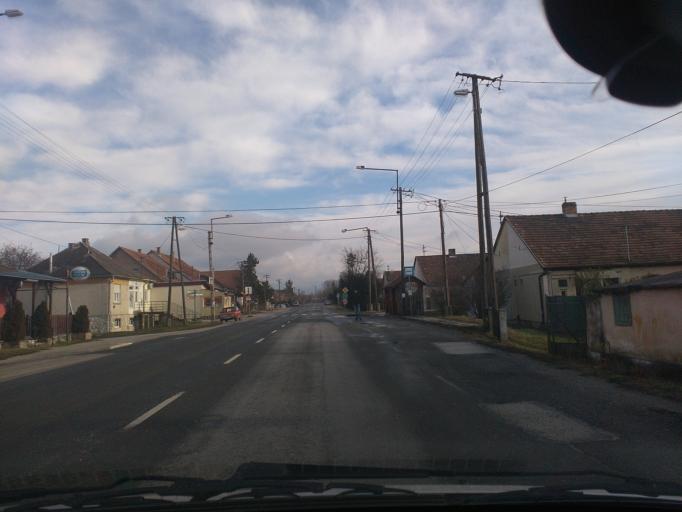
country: HU
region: Komarom-Esztergom
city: Tokod
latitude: 47.7363
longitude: 18.6708
